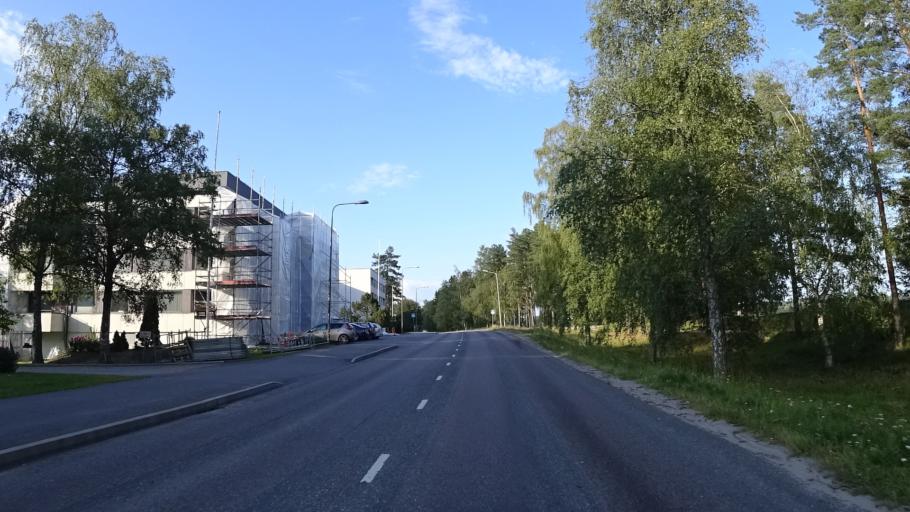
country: FI
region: South Karelia
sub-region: Imatra
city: Imatra
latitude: 61.1731
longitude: 28.7760
